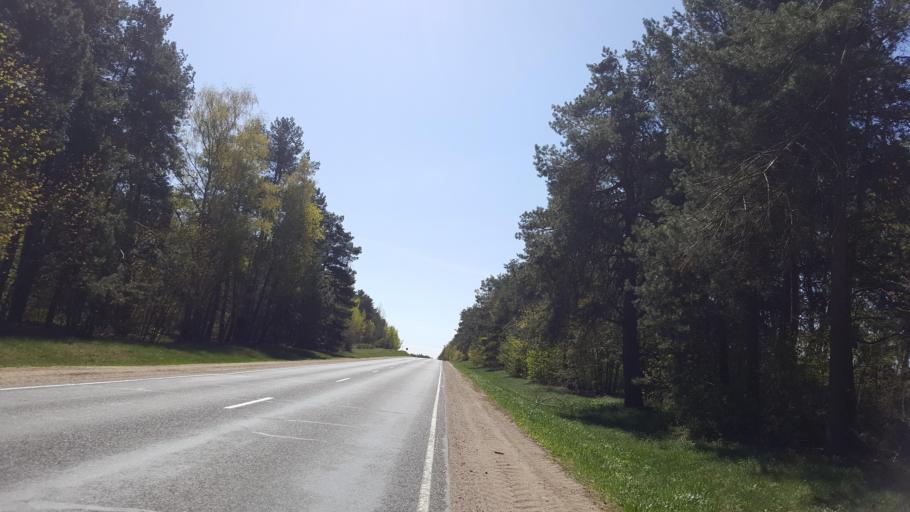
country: BY
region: Brest
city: Kamyanyets
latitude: 52.3511
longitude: 23.7772
